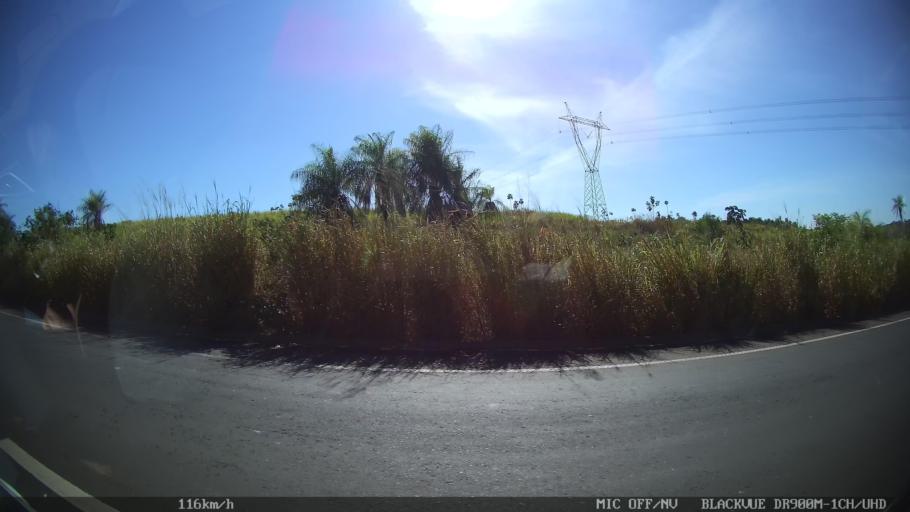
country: BR
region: Sao Paulo
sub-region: Olimpia
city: Olimpia
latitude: -20.6327
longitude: -48.8144
